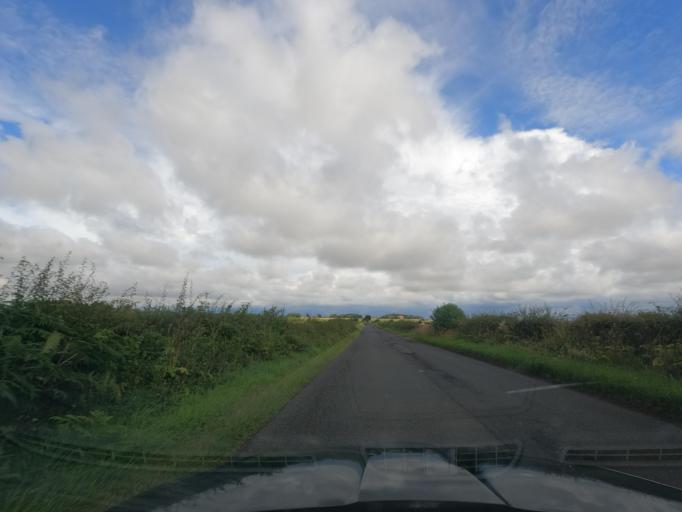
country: GB
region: England
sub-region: Northumberland
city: Lowick
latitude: 55.6331
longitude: -1.9904
